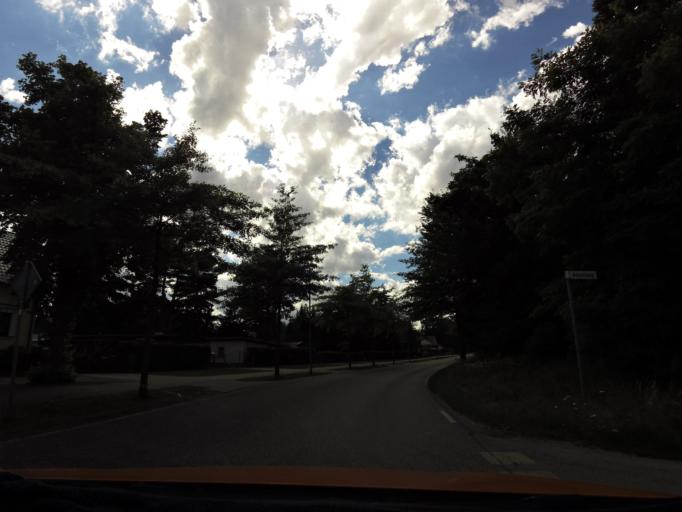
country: DE
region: Brandenburg
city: Bestensee
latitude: 52.2979
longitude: 13.7195
